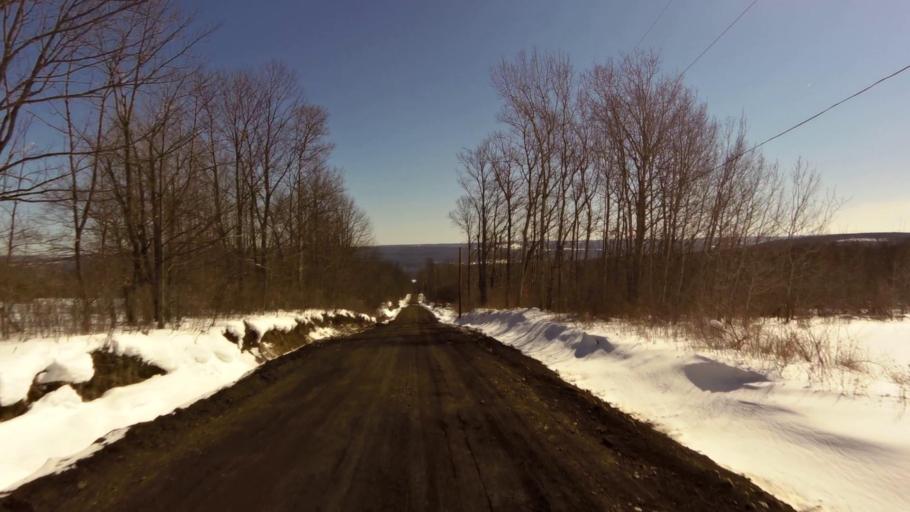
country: US
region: New York
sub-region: Allegany County
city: Houghton
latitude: 42.3593
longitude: -78.1710
